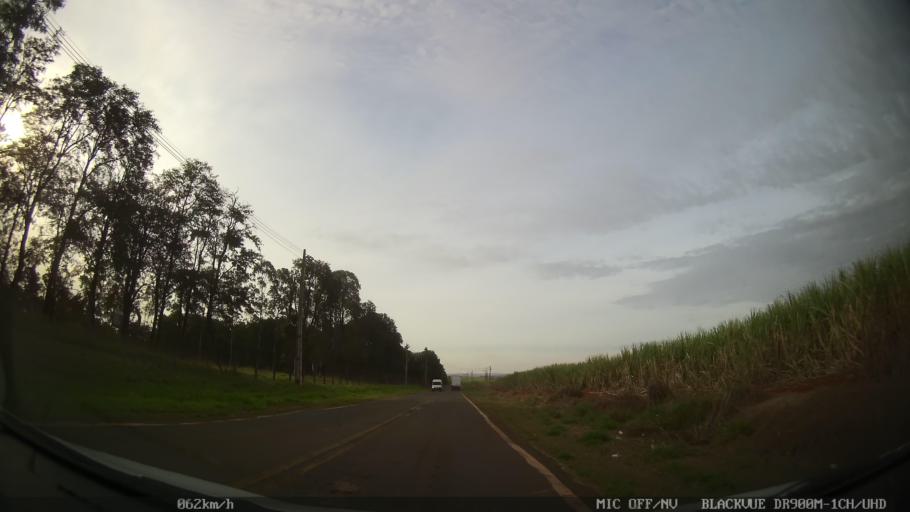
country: BR
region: Sao Paulo
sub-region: Piracicaba
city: Piracicaba
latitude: -22.7140
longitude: -47.5810
